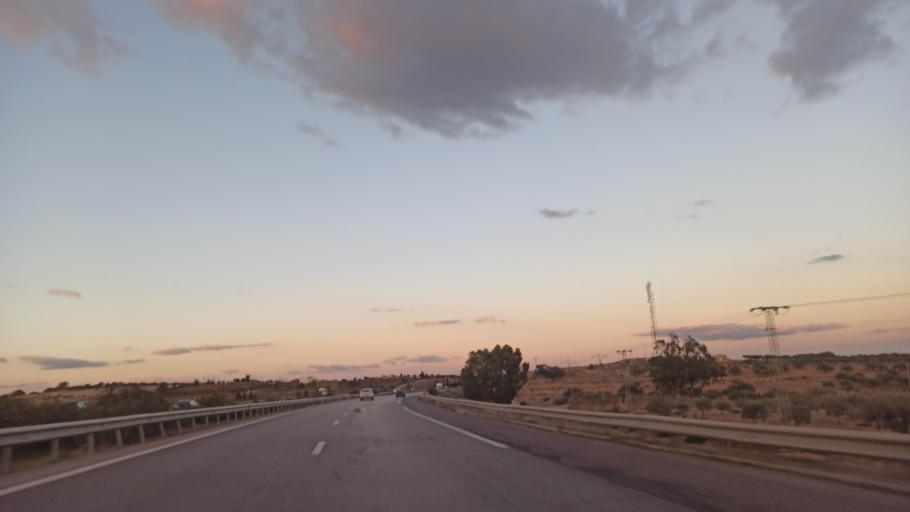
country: TN
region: Susah
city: Harqalah
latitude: 36.2356
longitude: 10.4143
